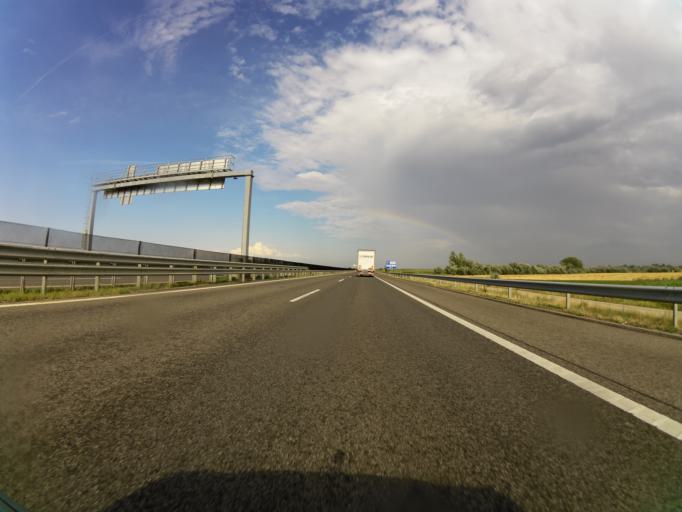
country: HU
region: Csongrad
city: Sandorfalva
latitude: 46.2960
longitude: 20.0974
